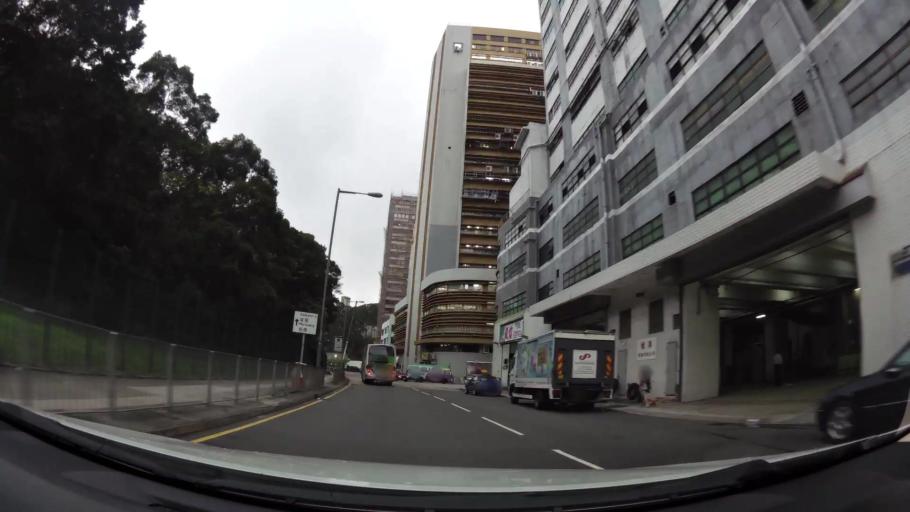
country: HK
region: Tsuen Wan
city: Tsuen Wan
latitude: 22.3580
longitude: 114.1198
